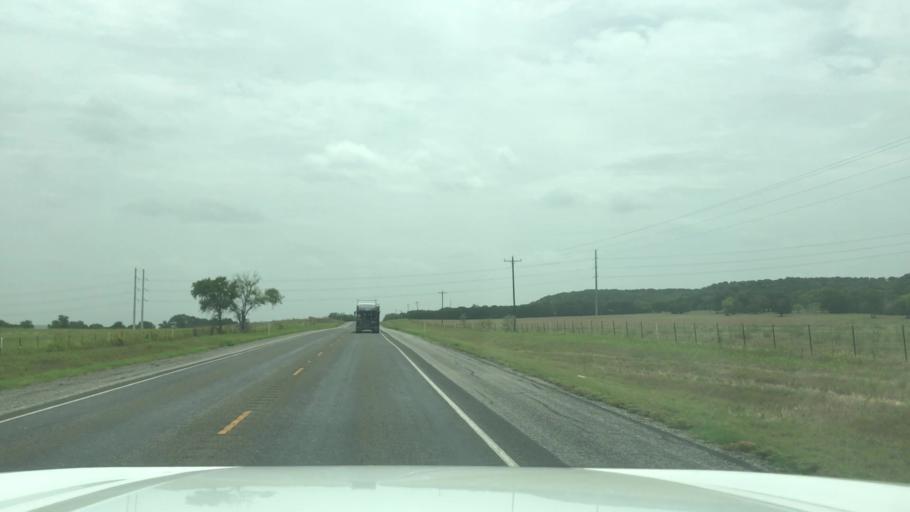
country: US
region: Texas
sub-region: Bosque County
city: Meridian
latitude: 31.8763
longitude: -97.6407
